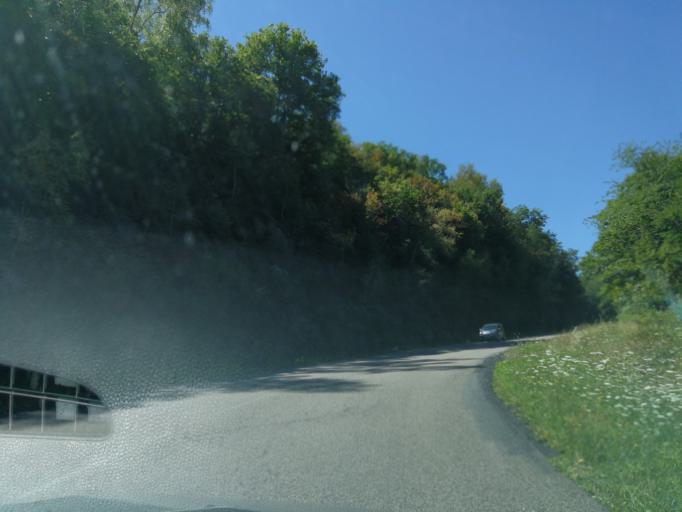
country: FR
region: Limousin
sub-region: Departement de la Correze
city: Argentat
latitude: 45.0619
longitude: 1.9469
